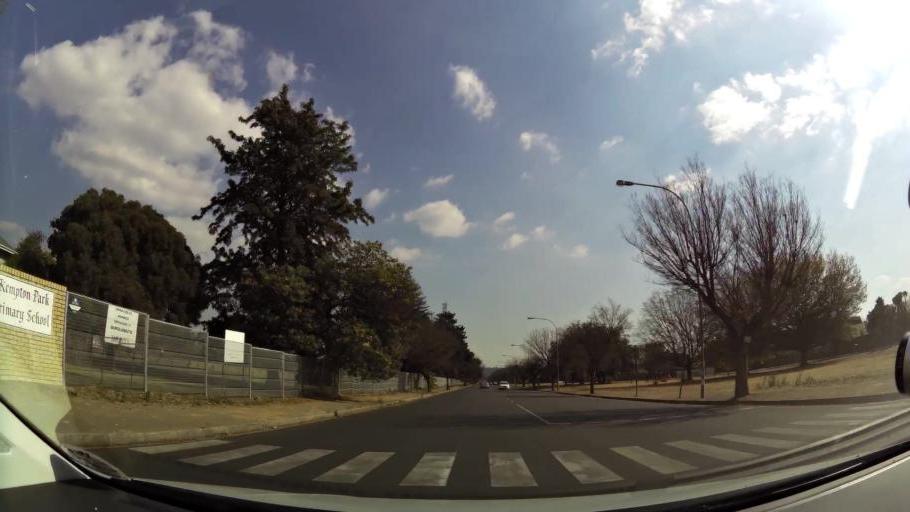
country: ZA
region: Gauteng
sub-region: City of Johannesburg Metropolitan Municipality
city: Modderfontein
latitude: -26.0949
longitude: 28.2340
